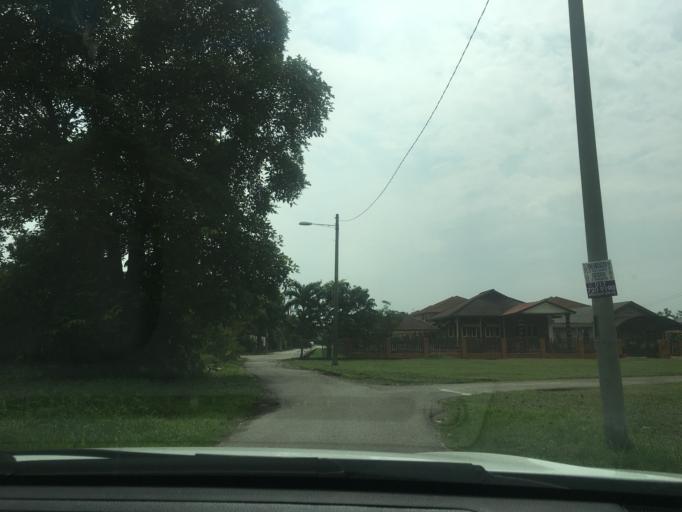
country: MY
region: Selangor
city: Klang
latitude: 3.0497
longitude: 101.4383
